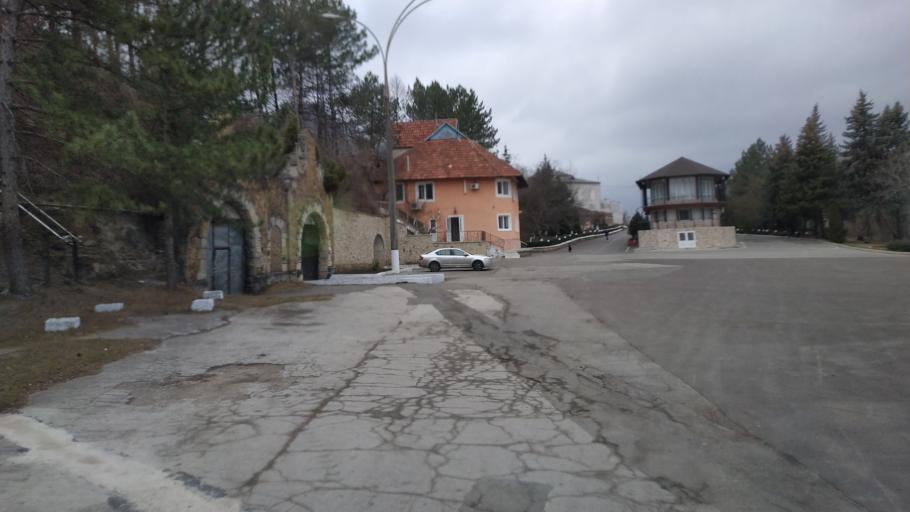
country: MD
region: Laloveni
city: Ialoveni
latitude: 46.9202
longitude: 28.8213
